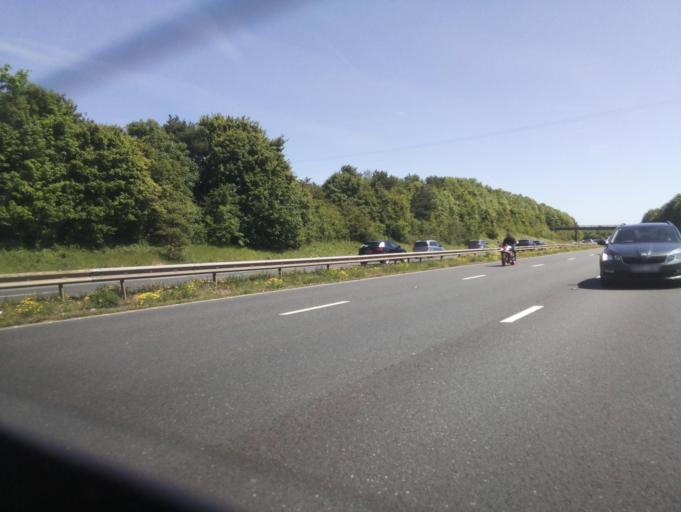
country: GB
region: England
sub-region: Somerset
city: Taunton
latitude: 50.9794
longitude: -3.1294
